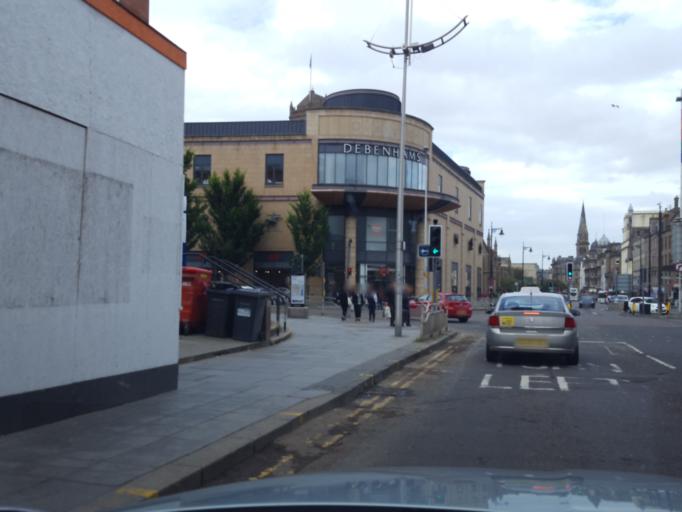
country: GB
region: Scotland
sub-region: Dundee City
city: Dundee
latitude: 56.4580
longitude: -2.9743
